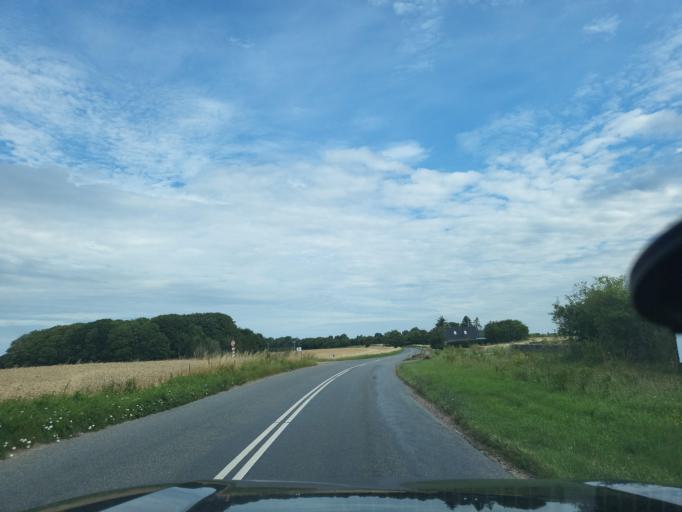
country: DK
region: Zealand
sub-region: Kalundborg Kommune
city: Svebolle
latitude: 55.7434
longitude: 11.3405
